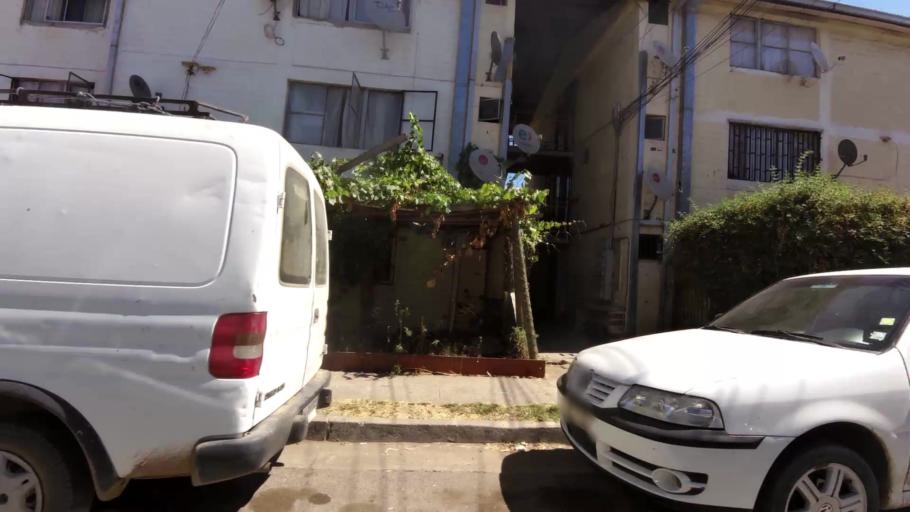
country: CL
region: O'Higgins
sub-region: Provincia de Colchagua
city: Chimbarongo
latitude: -34.5704
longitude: -70.9896
